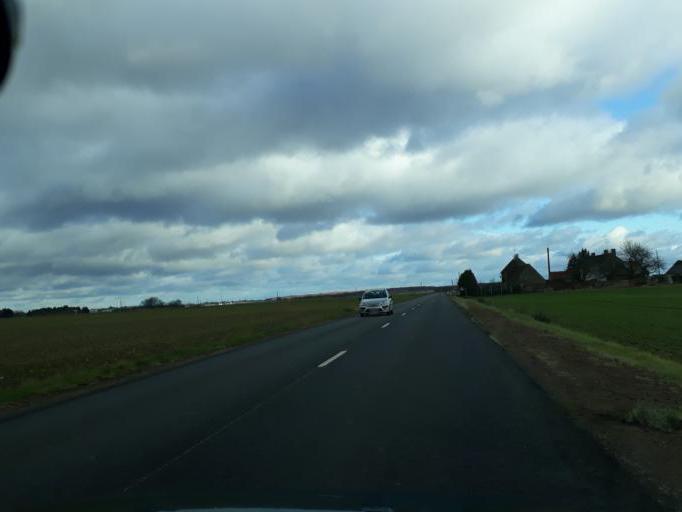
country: FR
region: Centre
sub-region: Departement du Loir-et-Cher
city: La Chaussee-Saint-Victor
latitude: 47.6378
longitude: 1.3611
